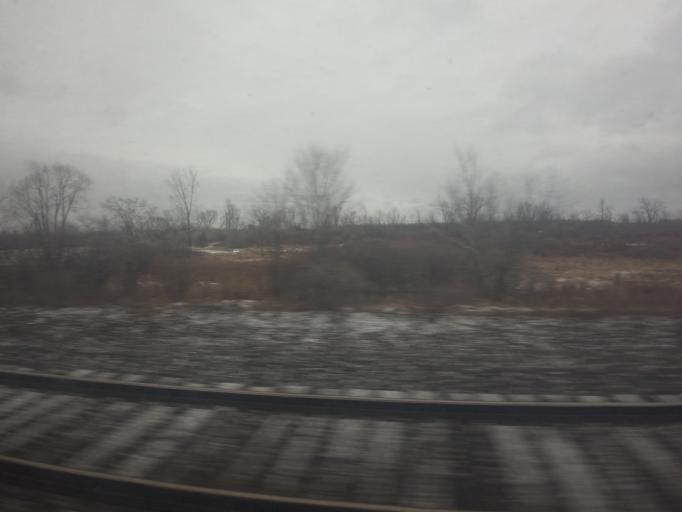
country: CA
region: Ontario
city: Gananoque
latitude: 44.3729
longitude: -76.1160
